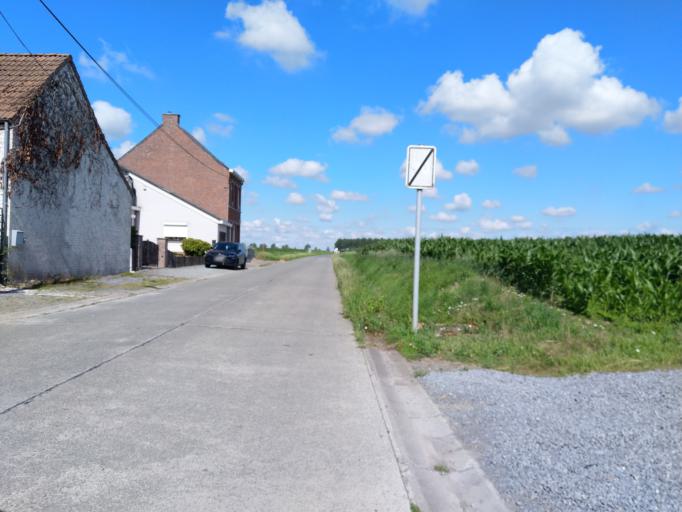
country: BE
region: Wallonia
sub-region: Province du Hainaut
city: Beloeil
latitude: 50.5921
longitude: 3.7431
